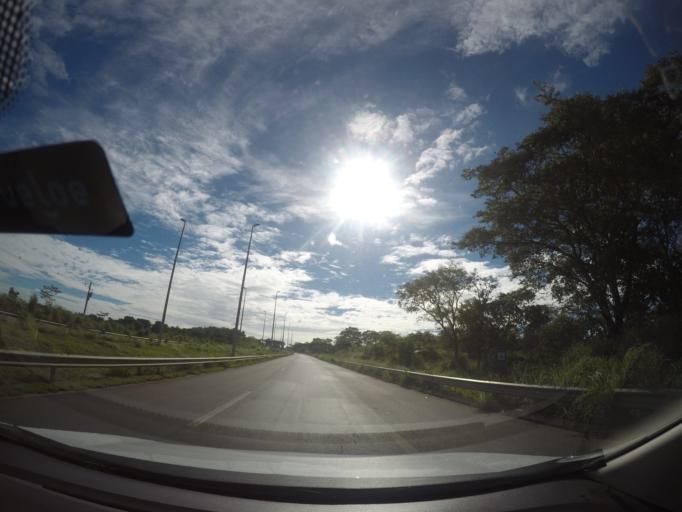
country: BR
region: Goias
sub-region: Senador Canedo
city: Senador Canedo
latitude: -16.6903
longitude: -49.1705
